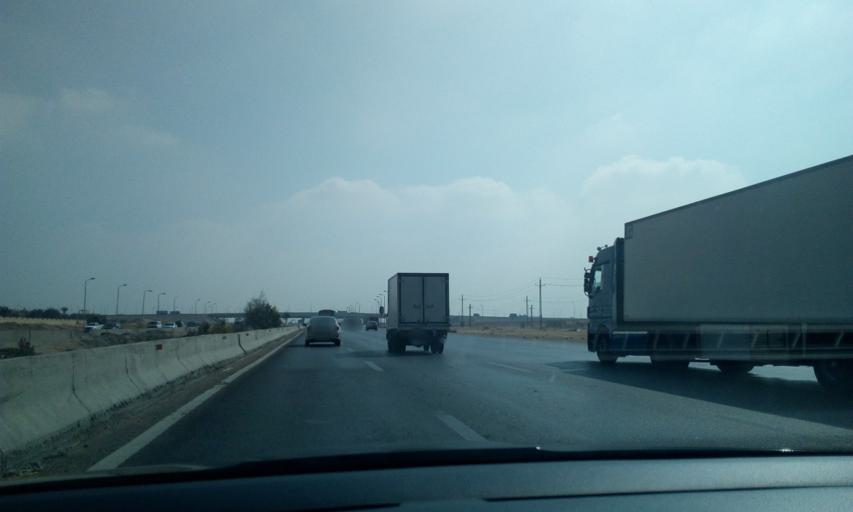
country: EG
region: Eastern Province
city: Bilbays
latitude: 30.2205
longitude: 31.6906
